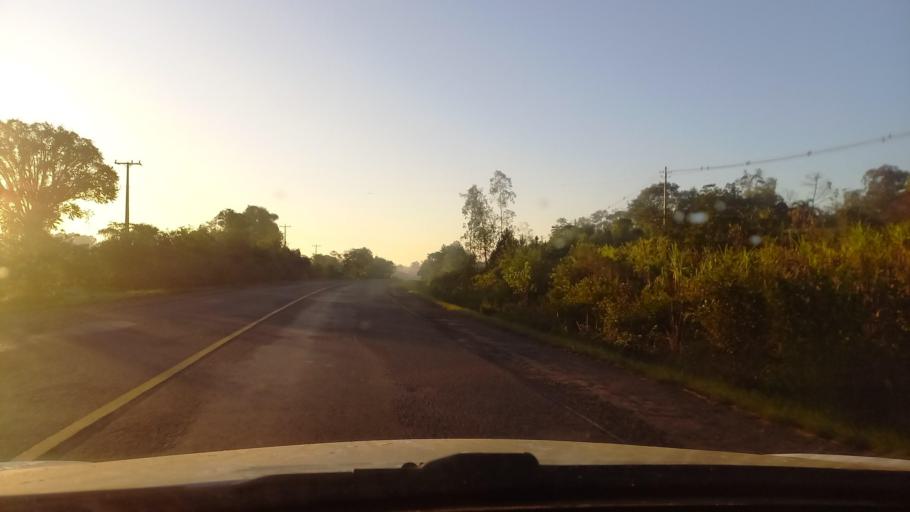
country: BR
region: Rio Grande do Sul
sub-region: Candelaria
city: Candelaria
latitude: -29.6807
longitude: -52.8227
